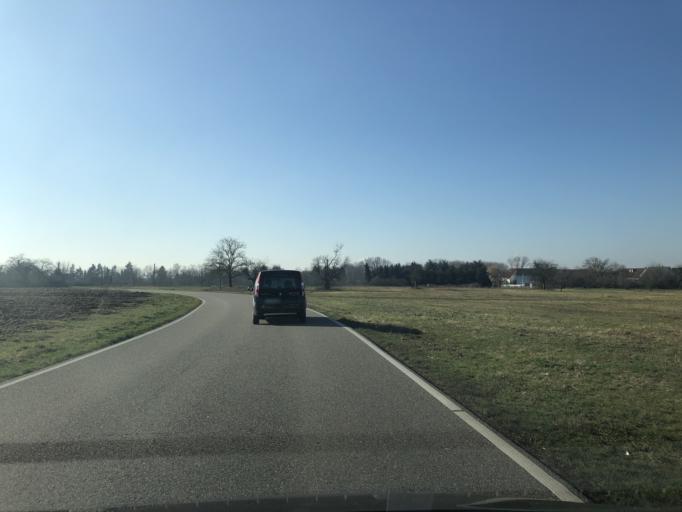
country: DE
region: Baden-Wuerttemberg
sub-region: Karlsruhe Region
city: Eggenstein-Leopoldshafen
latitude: 49.0725
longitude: 8.4001
